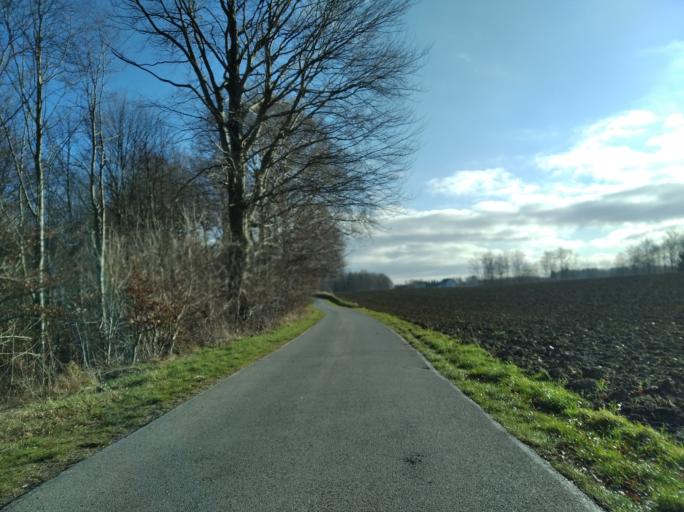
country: PL
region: Subcarpathian Voivodeship
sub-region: Powiat strzyzowski
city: Czudec
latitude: 49.9193
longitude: 21.8383
